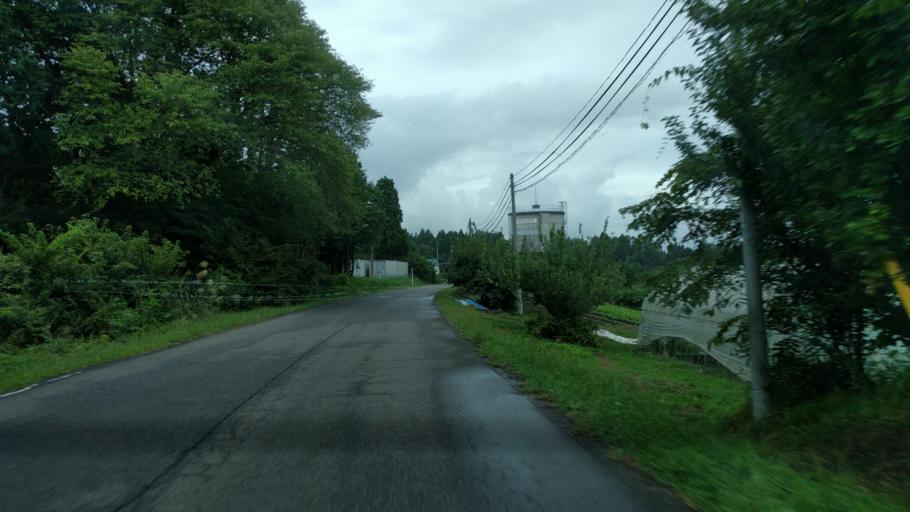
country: JP
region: Fukushima
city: Kitakata
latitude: 37.6074
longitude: 139.9254
